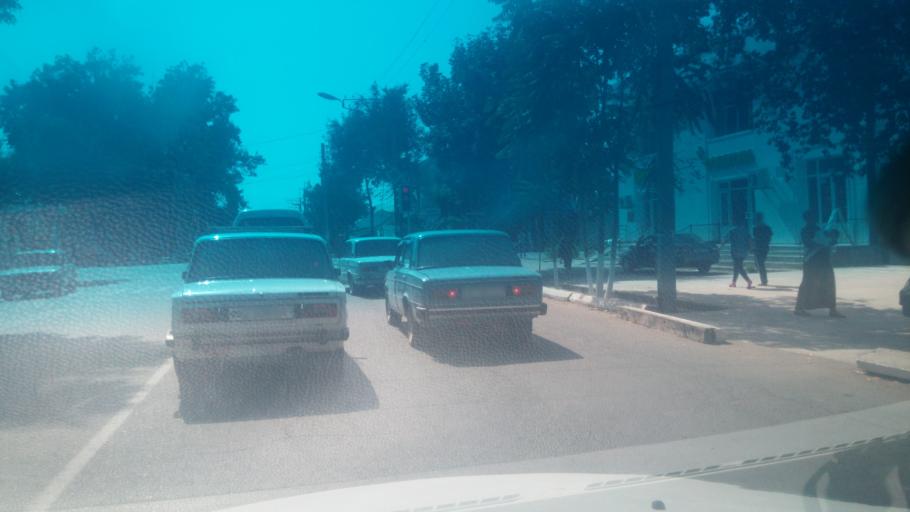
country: UZ
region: Sirdaryo
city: Sirdaryo
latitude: 40.8287
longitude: 68.6667
